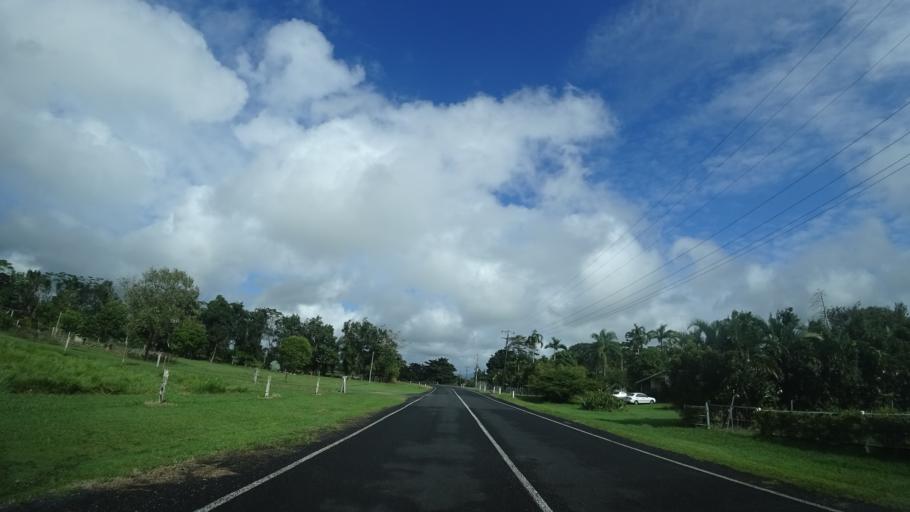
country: AU
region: Queensland
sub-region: Cassowary Coast
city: Innisfail
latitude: -17.5832
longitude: 146.0682
